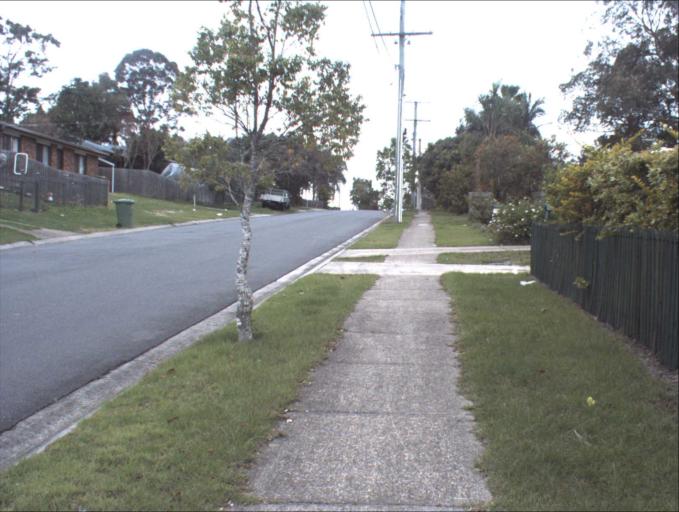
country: AU
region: Queensland
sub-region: Logan
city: Waterford West
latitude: -27.6898
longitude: 153.1002
